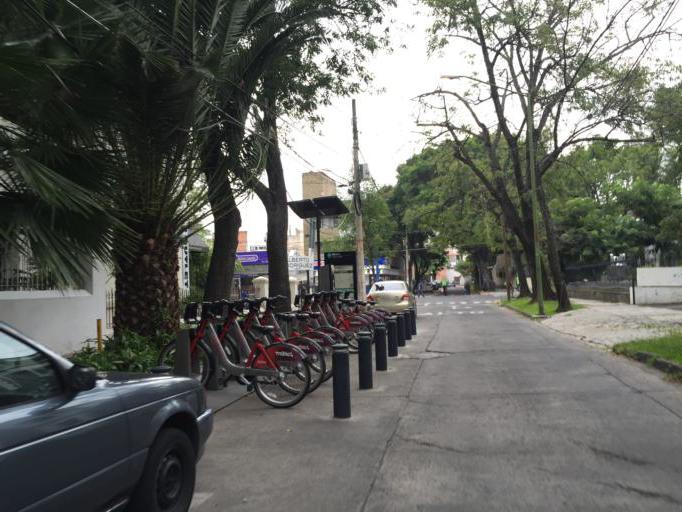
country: MX
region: Jalisco
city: Guadalajara
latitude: 20.6753
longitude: -103.3651
